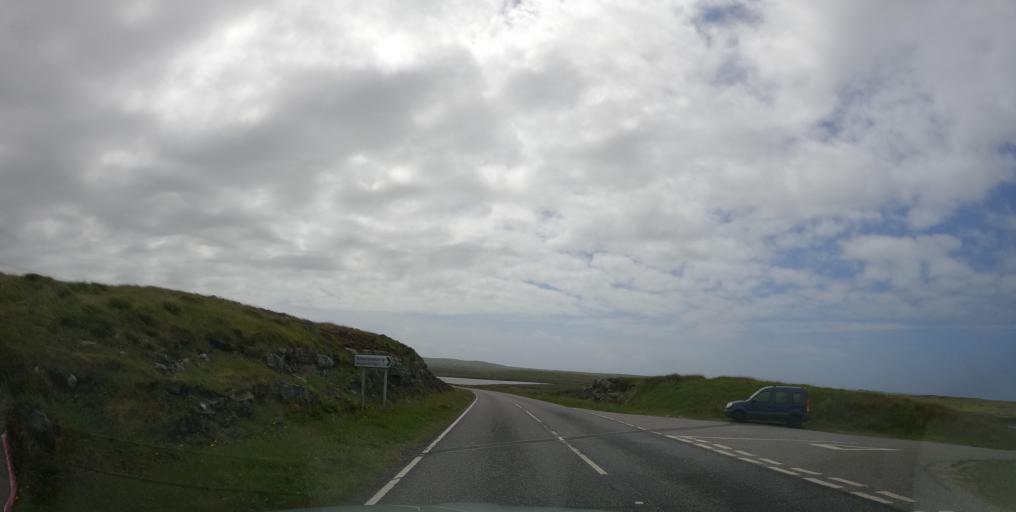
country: GB
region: Scotland
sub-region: Eilean Siar
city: Isle of South Uist
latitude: 57.2692
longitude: -7.3675
